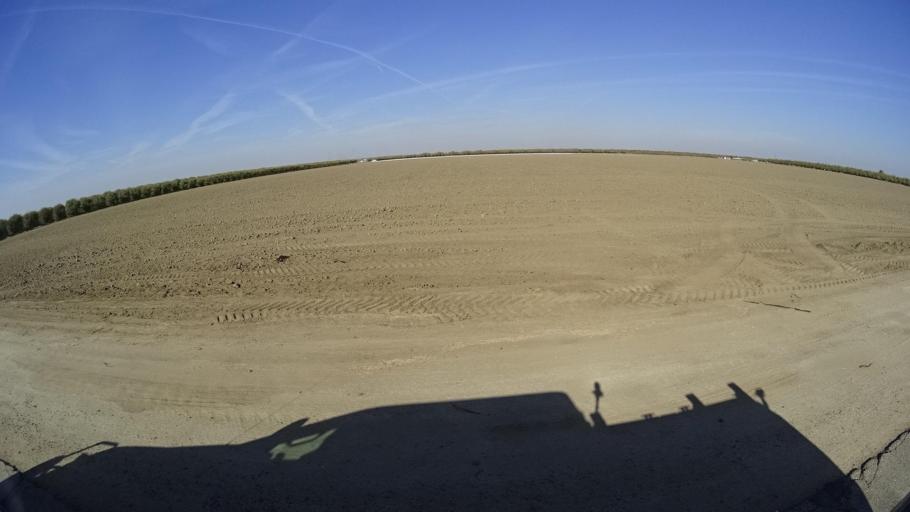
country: US
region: California
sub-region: Kern County
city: Wasco
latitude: 35.6671
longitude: -119.3786
